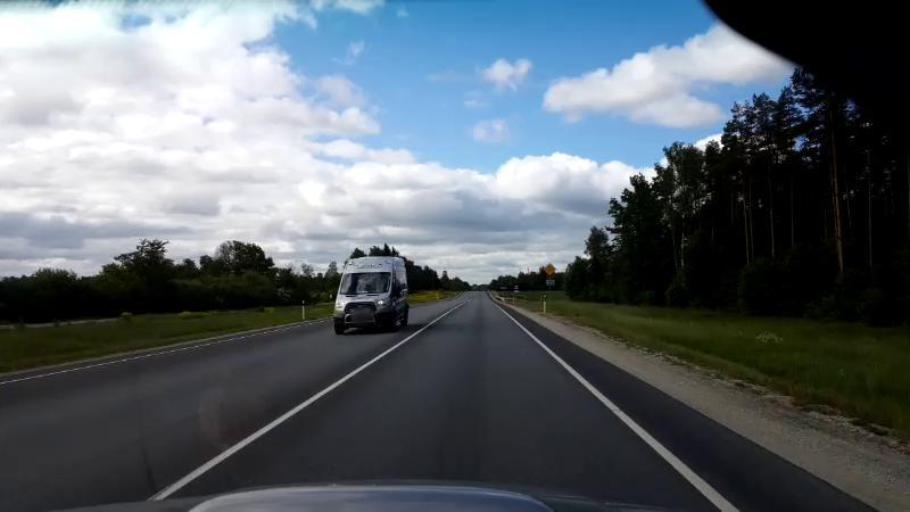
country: EE
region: Harju
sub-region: Nissi vald
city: Riisipere
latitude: 59.0591
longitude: 24.4479
